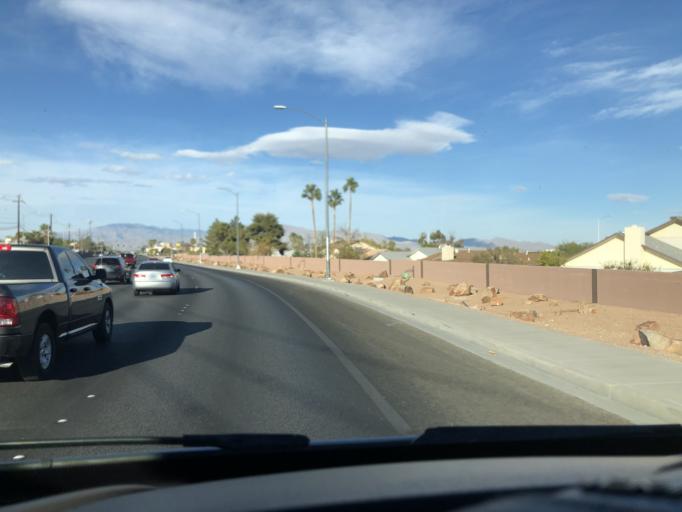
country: US
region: Nevada
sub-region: Clark County
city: Spring Valley
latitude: 36.1626
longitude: -115.2599
